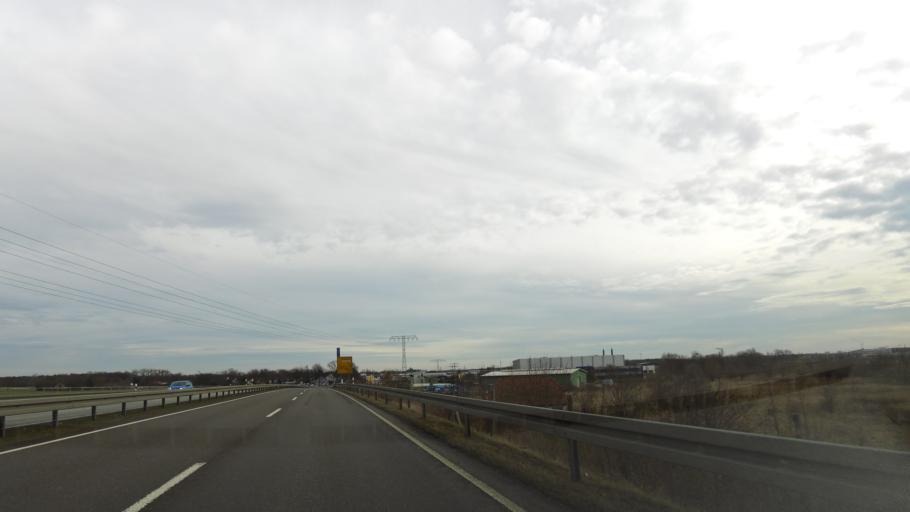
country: DE
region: Brandenburg
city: Petershagen
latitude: 52.4943
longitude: 13.7746
